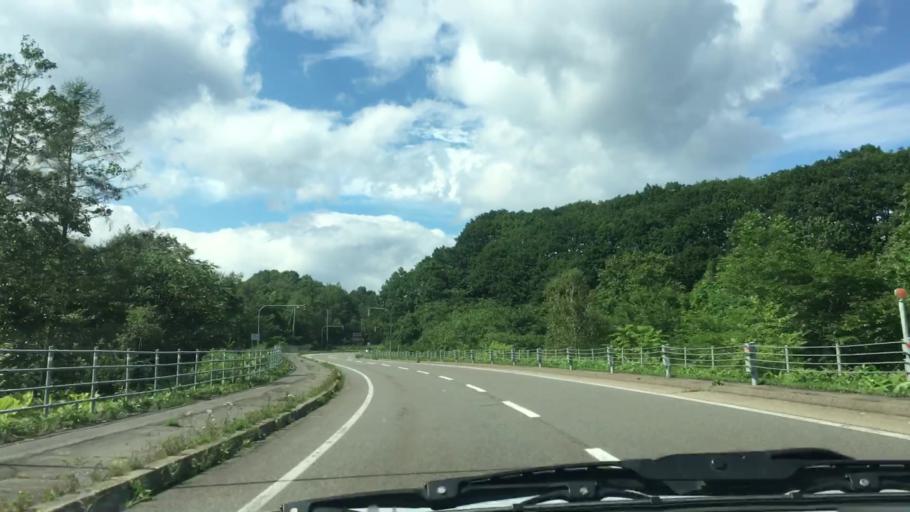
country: JP
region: Hokkaido
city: Otofuke
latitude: 43.3346
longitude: 143.2898
